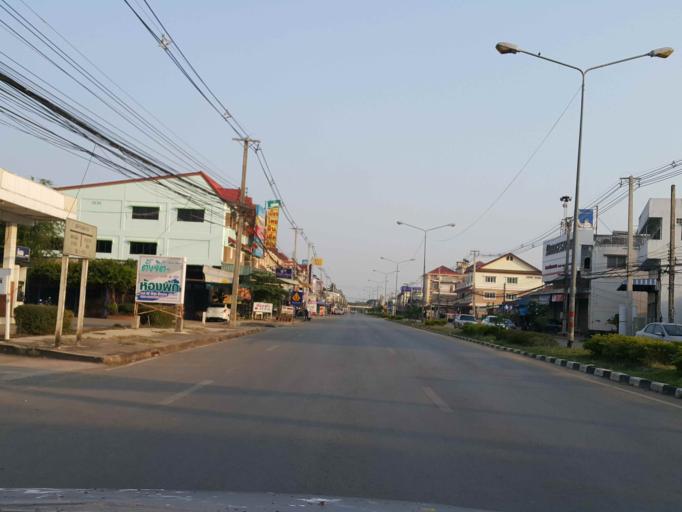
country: TH
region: Sukhothai
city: Sawankhalok
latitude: 17.3021
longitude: 99.8342
